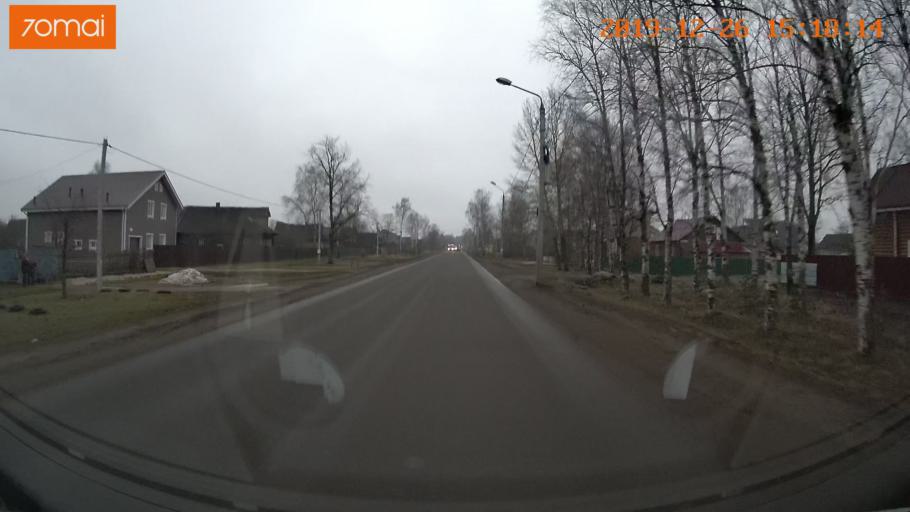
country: RU
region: Jaroslavl
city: Rybinsk
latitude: 58.0711
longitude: 38.8436
